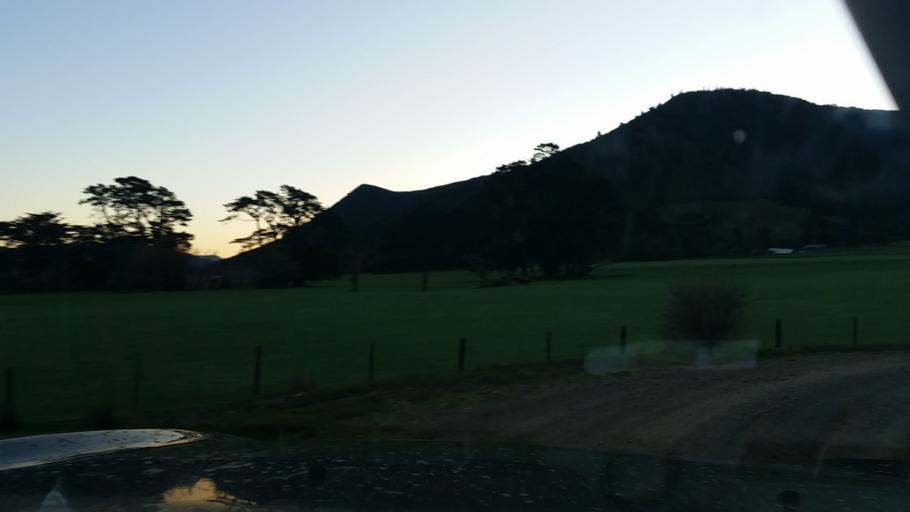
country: NZ
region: Marlborough
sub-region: Marlborough District
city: Picton
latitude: -41.1587
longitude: 174.1337
